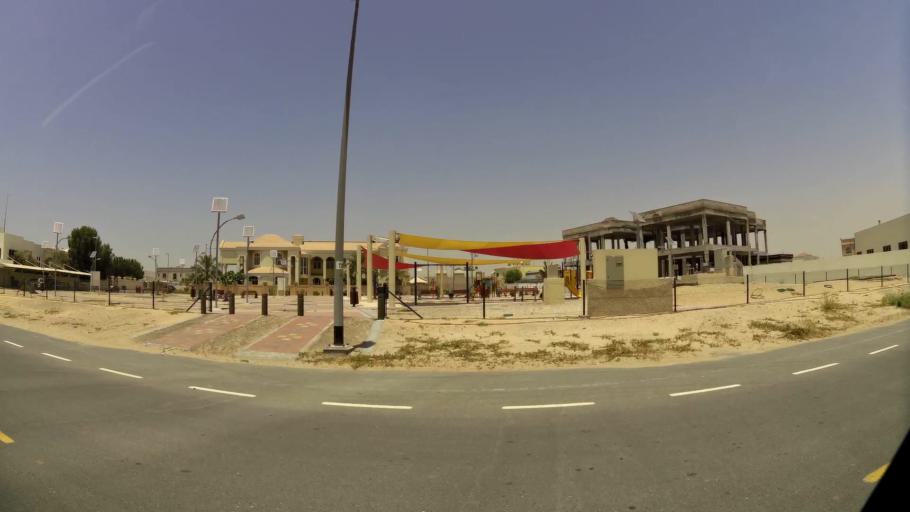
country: AE
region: Dubai
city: Dubai
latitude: 25.0913
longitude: 55.1907
